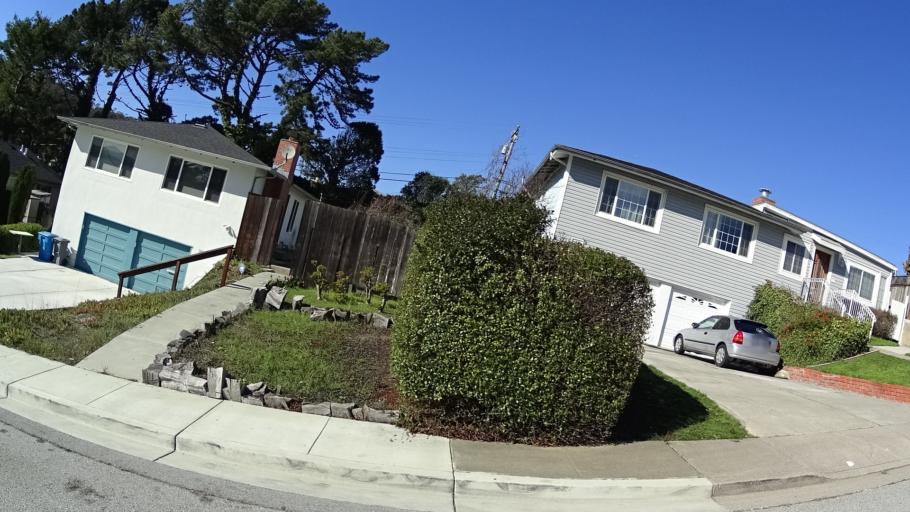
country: US
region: California
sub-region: San Mateo County
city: San Bruno
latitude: 37.6284
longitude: -122.4485
